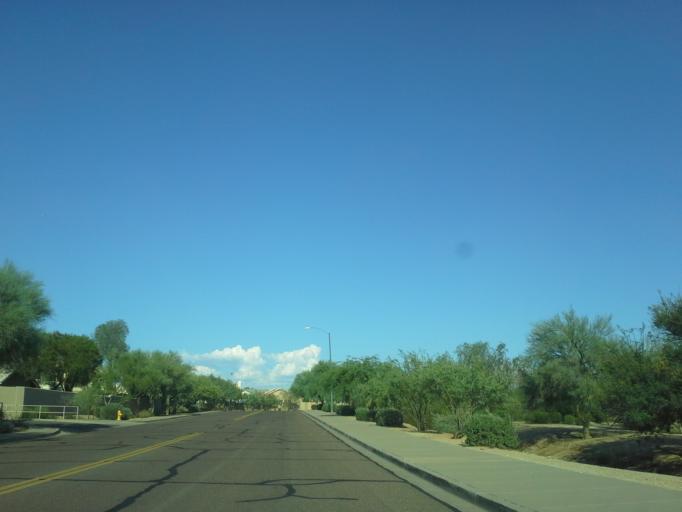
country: US
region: Arizona
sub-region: Maricopa County
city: Cave Creek
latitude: 33.7661
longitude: -111.9952
